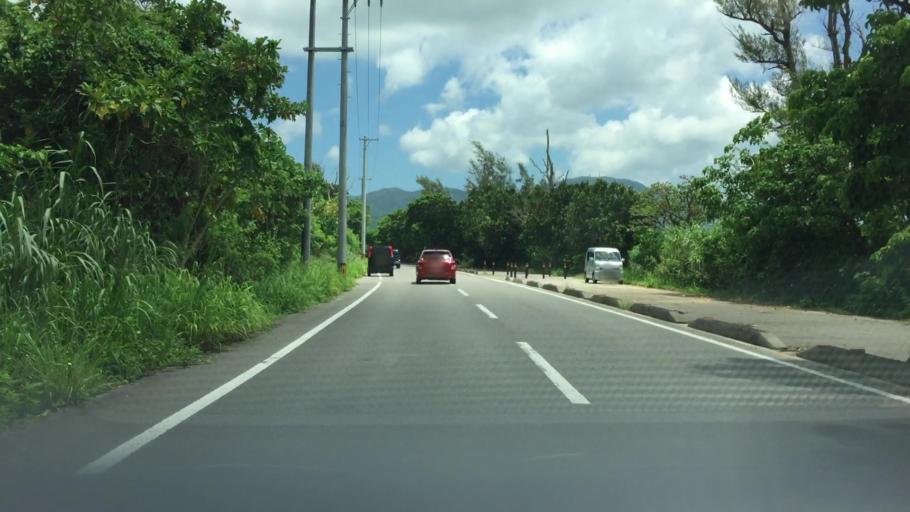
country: JP
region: Okinawa
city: Ishigaki
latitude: 24.3864
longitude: 124.1388
